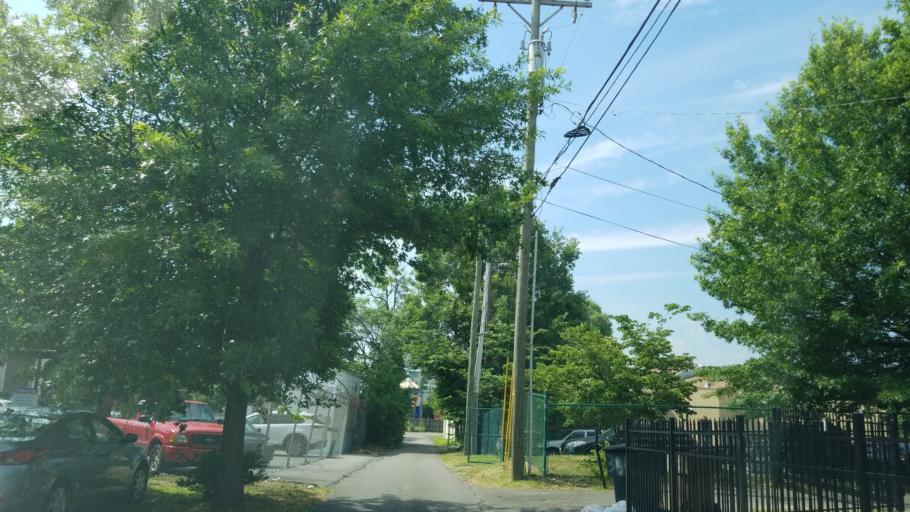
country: US
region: Tennessee
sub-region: Davidson County
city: Nashville
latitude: 36.1592
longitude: -86.7935
